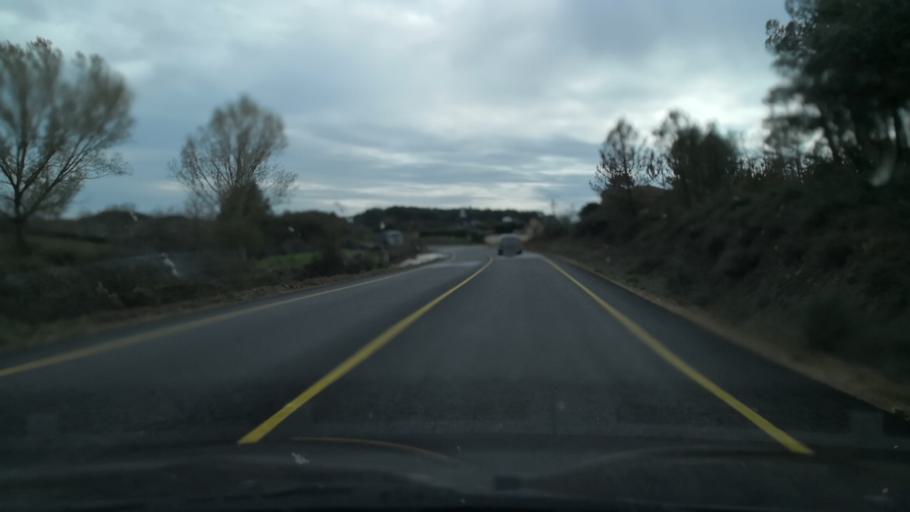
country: ES
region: Castille and Leon
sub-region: Provincia de Salamanca
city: Robleda
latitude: 40.3773
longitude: -6.6128
